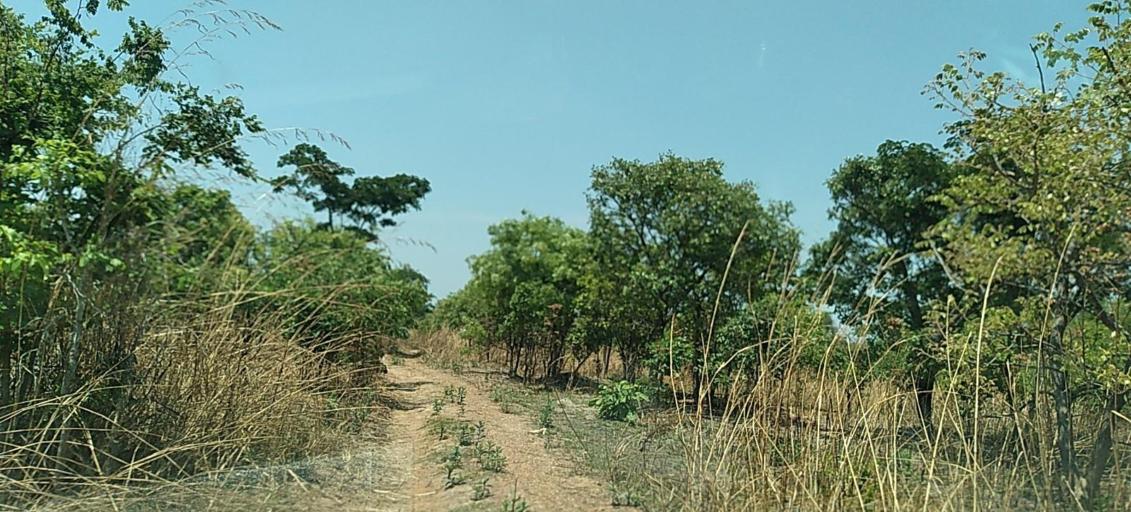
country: ZM
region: Copperbelt
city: Luanshya
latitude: -12.9832
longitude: 28.3285
